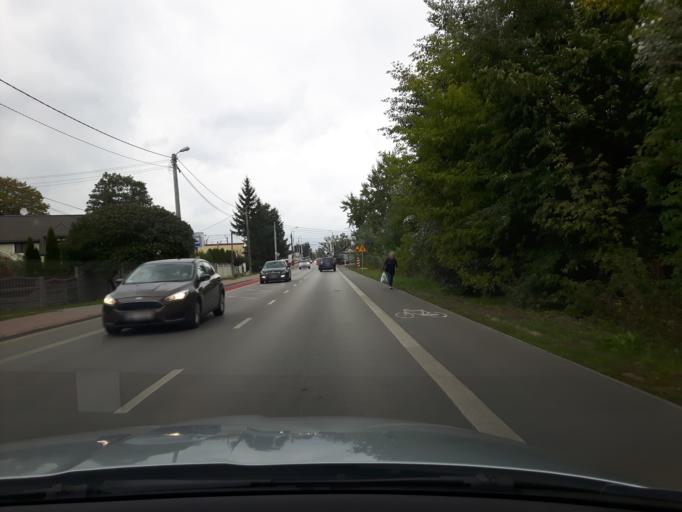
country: PL
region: Masovian Voivodeship
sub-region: Powiat wolominski
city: Kobylka
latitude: 52.3247
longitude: 21.1909
